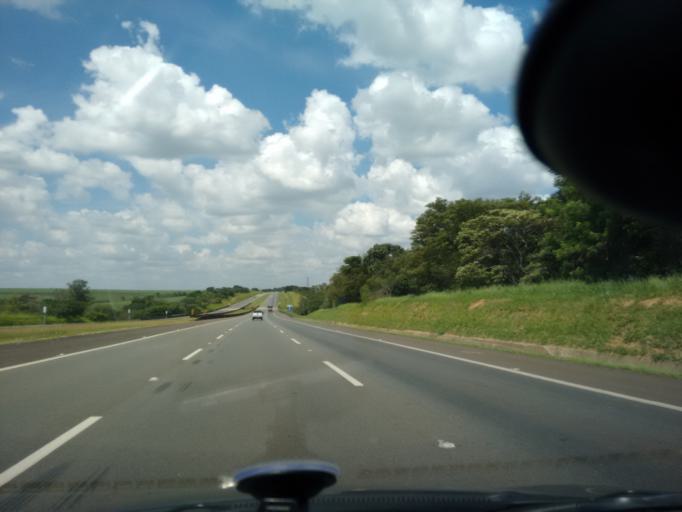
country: BR
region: Sao Paulo
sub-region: Santa Barbara D'Oeste
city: Santa Barbara d'Oeste
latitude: -22.7965
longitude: -47.4096
